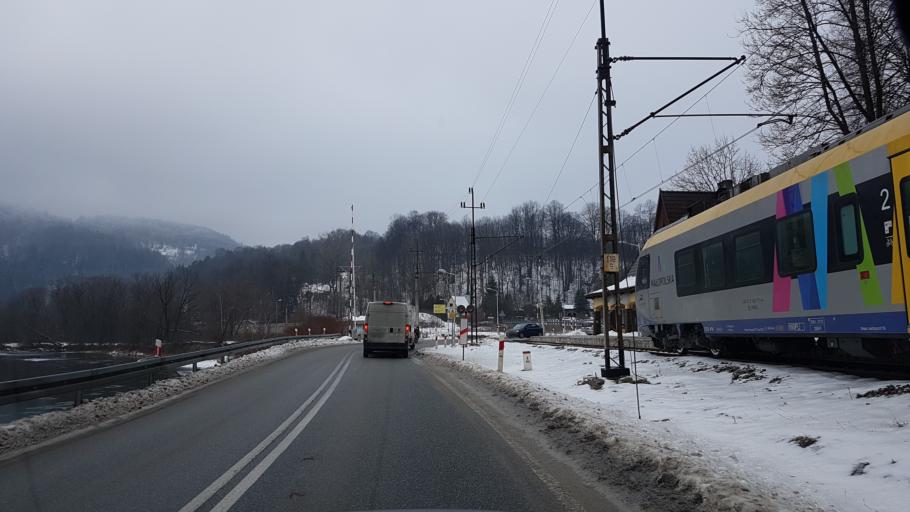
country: PL
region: Lesser Poland Voivodeship
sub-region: Powiat nowosadecki
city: Piwniczna-Zdroj
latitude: 49.4023
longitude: 20.7557
